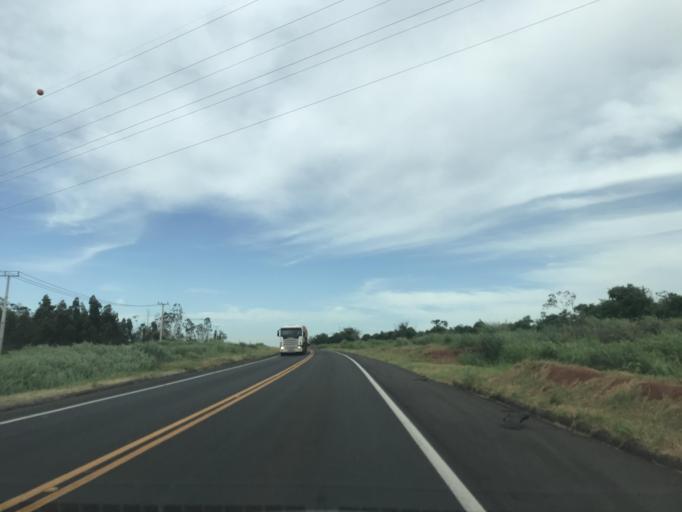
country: BR
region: Parana
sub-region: Paranavai
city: Paranavai
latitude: -23.0141
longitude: -52.5155
